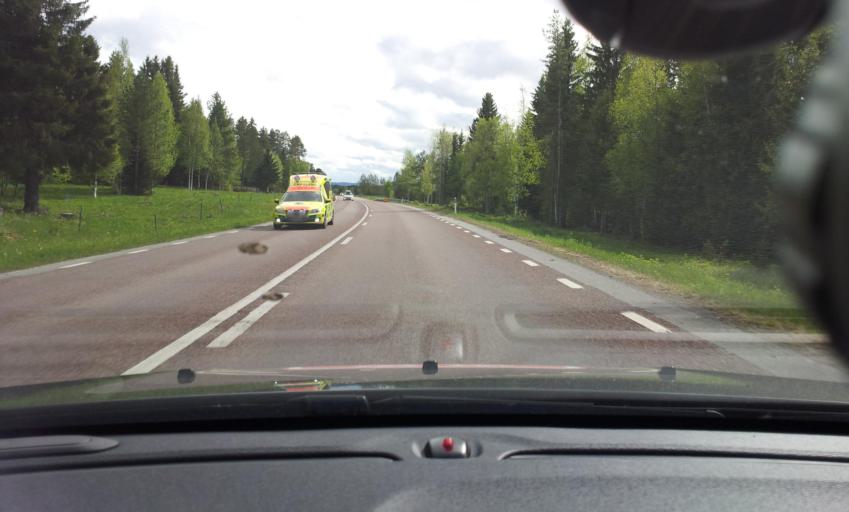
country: SE
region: Jaemtland
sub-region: Bergs Kommun
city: Hoverberg
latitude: 62.9805
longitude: 14.5679
